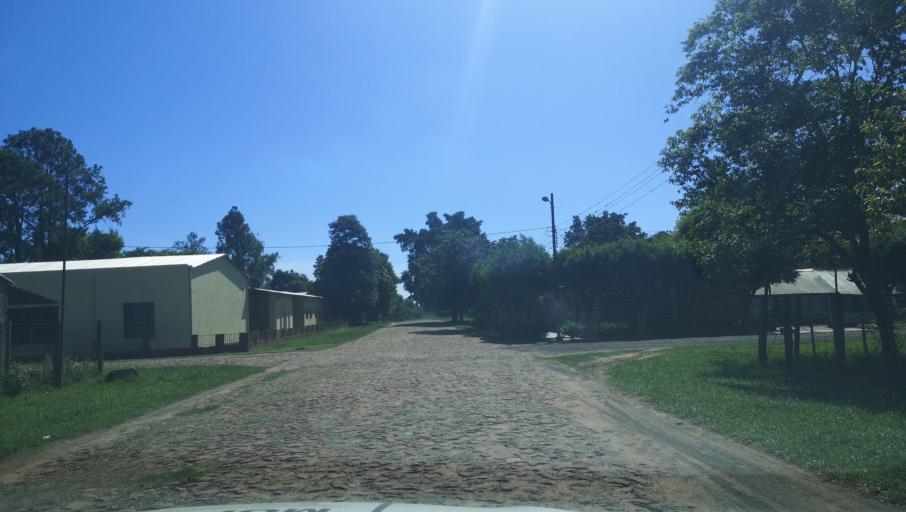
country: PY
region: Caaguazu
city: Carayao
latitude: -25.1947
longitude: -56.4017
